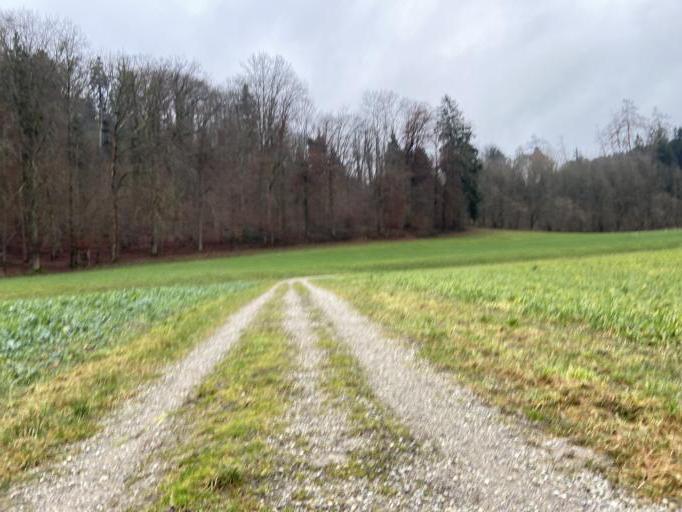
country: CH
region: Zurich
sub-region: Bezirk Winterthur
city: Wuelflingen (Kreis 6) / Niederfeld
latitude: 47.4943
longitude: 8.6794
